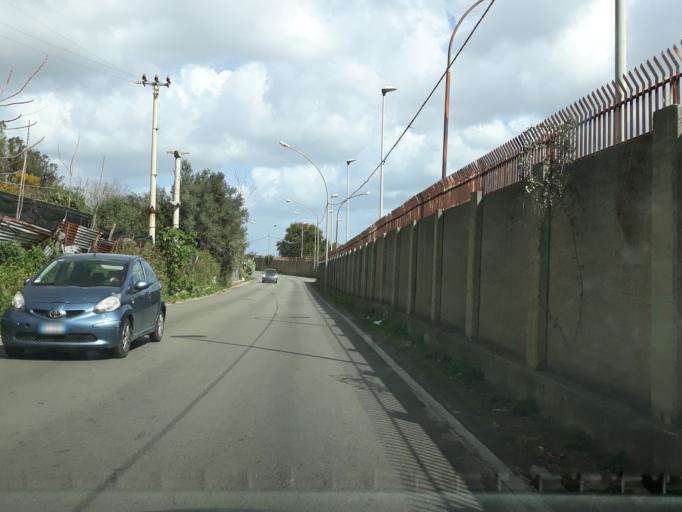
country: IT
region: Sicily
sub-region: Palermo
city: Monreale
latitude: 38.1008
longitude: 13.3103
